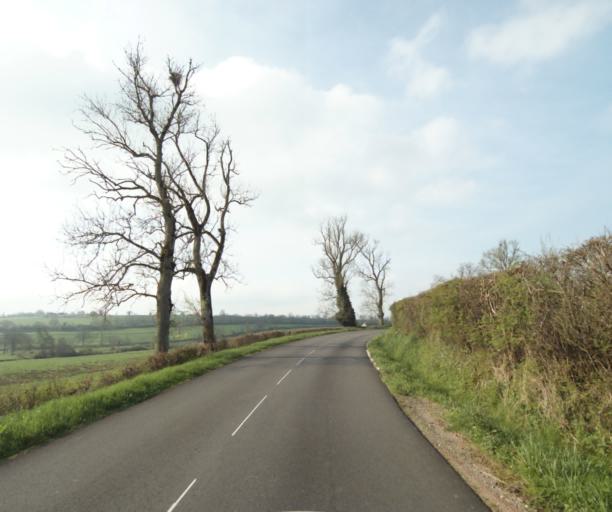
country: FR
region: Bourgogne
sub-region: Departement de Saone-et-Loire
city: Charolles
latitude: 46.4113
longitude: 4.2191
